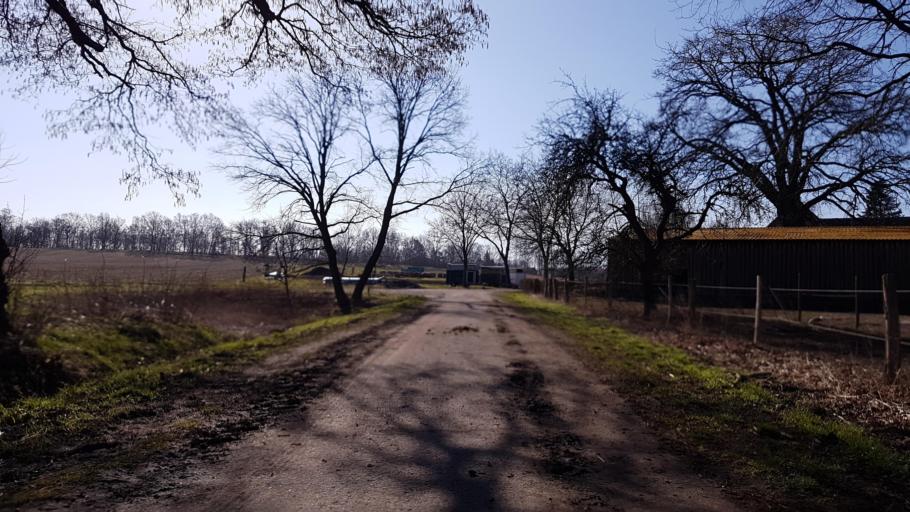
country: DE
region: Lower Saxony
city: Garbsen-Mitte
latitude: 52.4498
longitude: 9.6380
